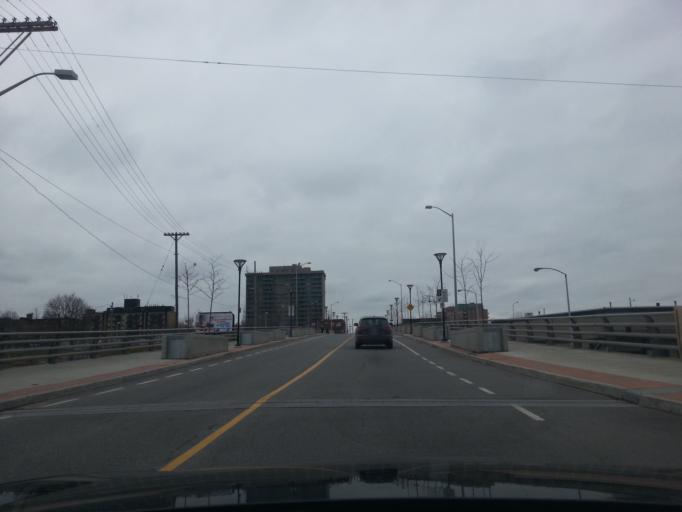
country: CA
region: Ontario
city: Ottawa
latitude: 45.4076
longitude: -75.7168
